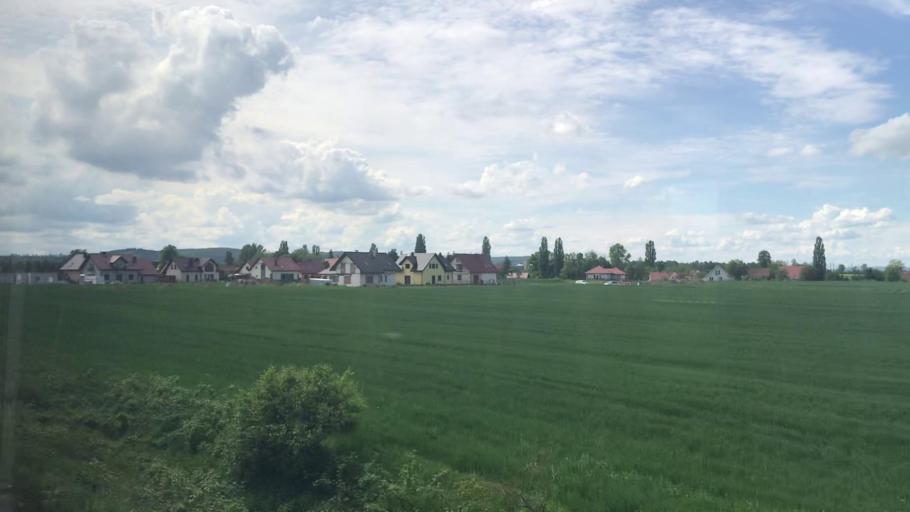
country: PL
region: Lower Silesian Voivodeship
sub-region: Powiat swidnicki
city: Swiebodzice
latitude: 50.8721
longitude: 16.3564
